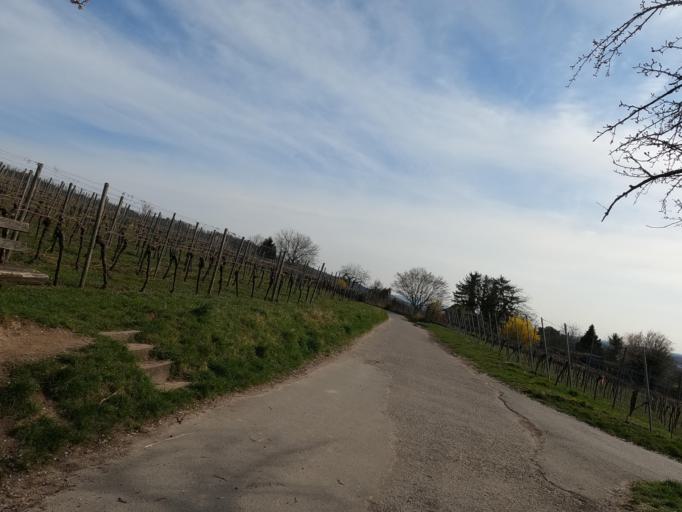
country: DE
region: Baden-Wuerttemberg
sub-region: Karlsruhe Region
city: Laudenbach
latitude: 49.6293
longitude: 8.6455
